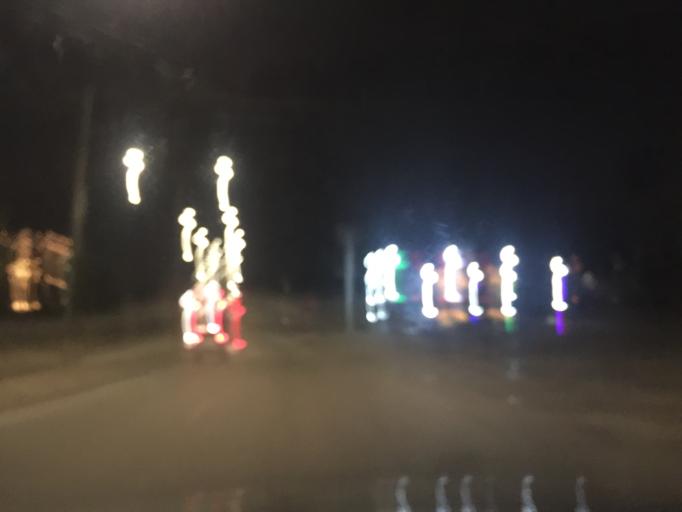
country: JO
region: Amman
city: Umm as Summaq
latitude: 31.8724
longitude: 35.8371
